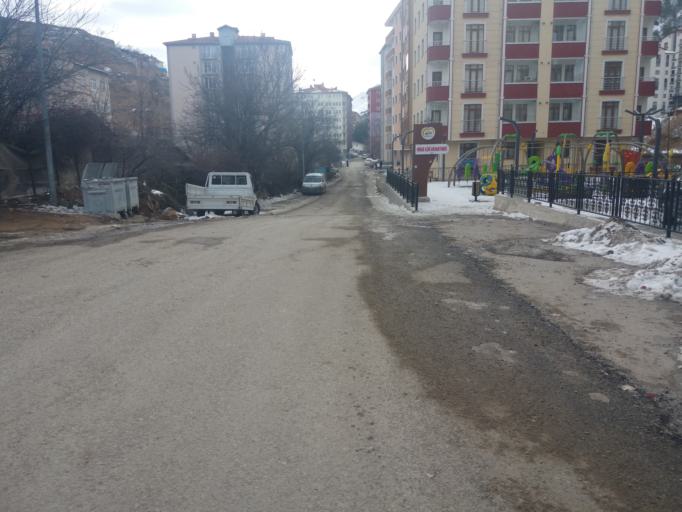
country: TR
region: Gumushane
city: Gumushkhane
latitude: 40.4537
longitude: 39.4917
